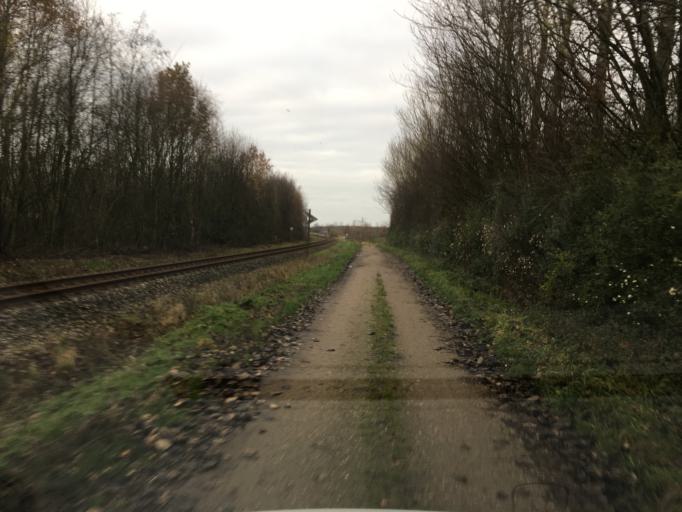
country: DK
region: South Denmark
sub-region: Tonder Kommune
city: Tonder
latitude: 54.9497
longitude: 8.8567
